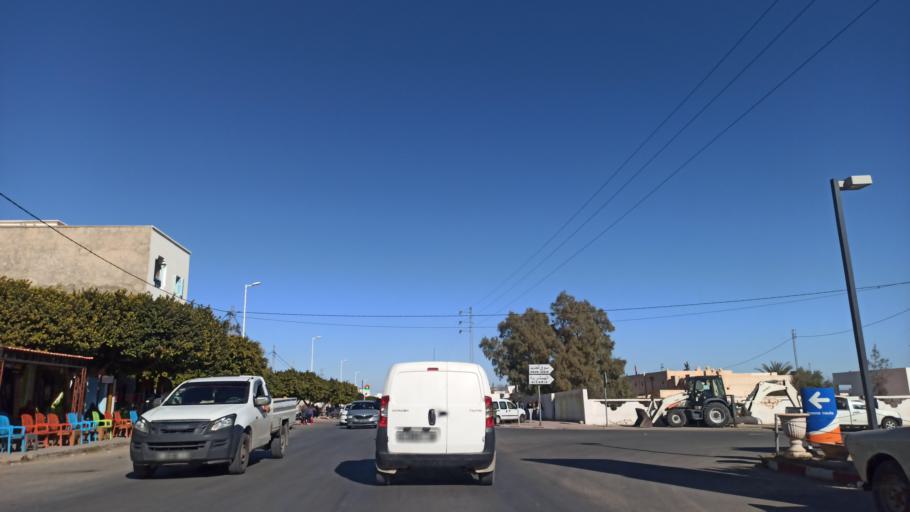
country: TN
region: Sidi Bu Zayd
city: Bi'r al Hufayy
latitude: 34.9283
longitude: 9.1929
